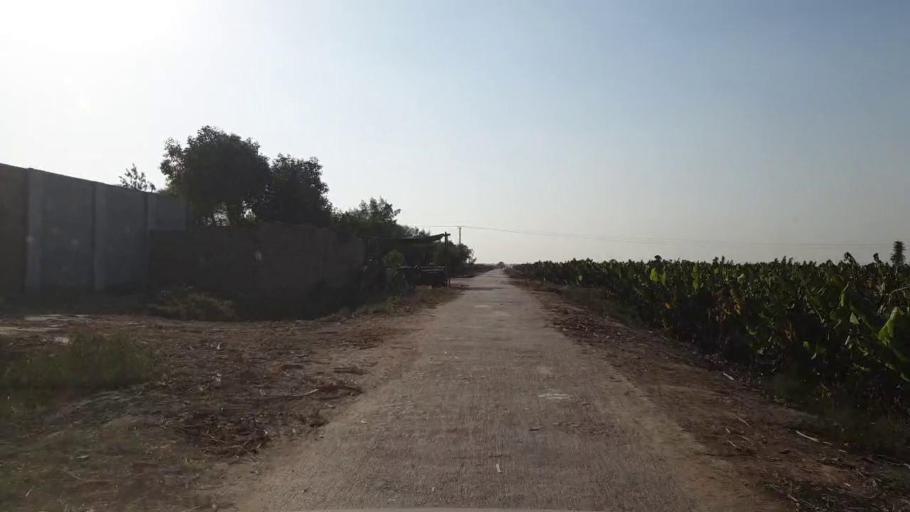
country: PK
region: Sindh
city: Tando Allahyar
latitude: 25.3467
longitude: 68.6824
